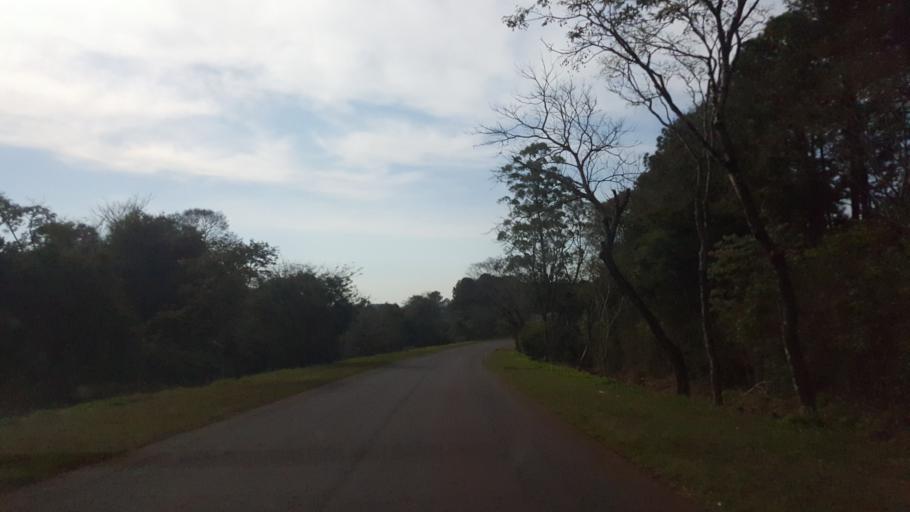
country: AR
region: Misiones
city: Capiovi
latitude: -26.9332
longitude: -55.0888
